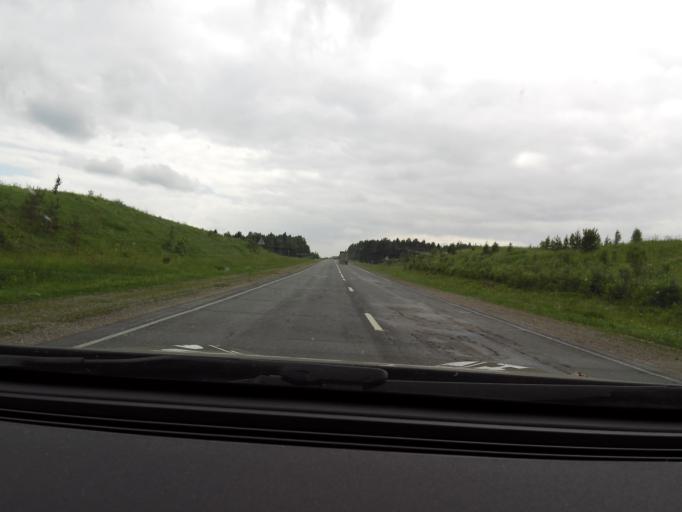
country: RU
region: Perm
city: Suksun
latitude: 57.1408
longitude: 57.2960
